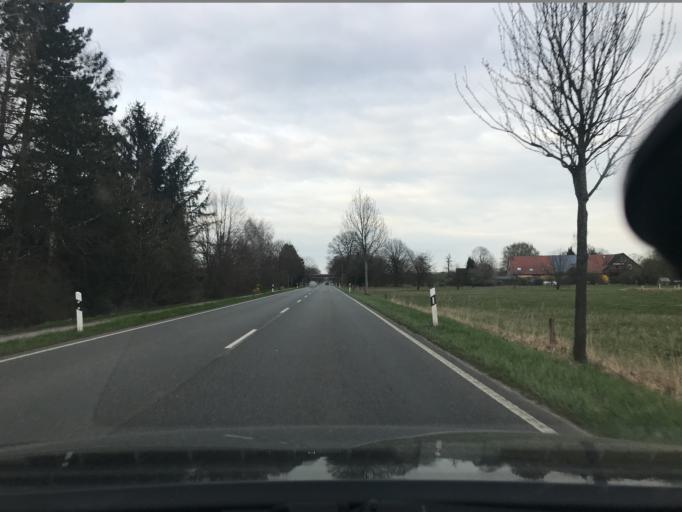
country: DE
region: North Rhine-Westphalia
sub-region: Regierungsbezirk Dusseldorf
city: Wesel
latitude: 51.6948
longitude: 6.6633
